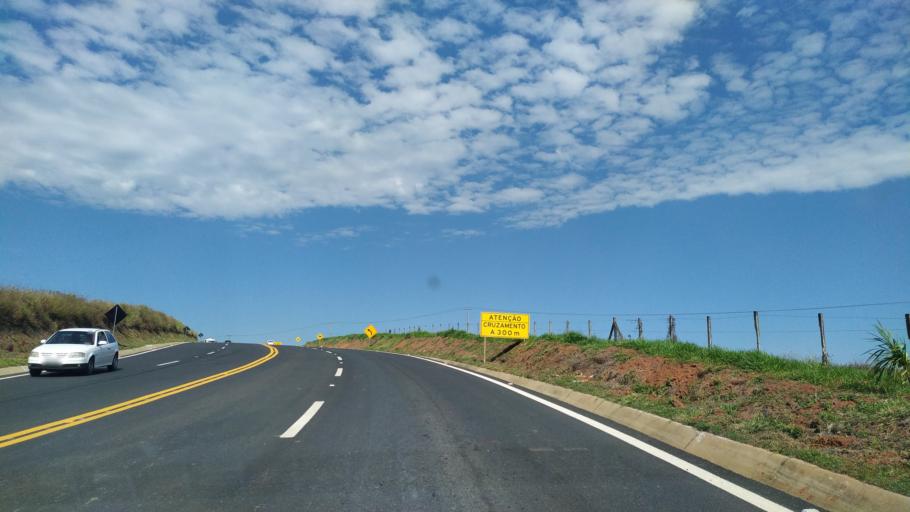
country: BR
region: Parana
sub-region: Telemaco Borba
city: Telemaco Borba
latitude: -24.2792
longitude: -50.7138
